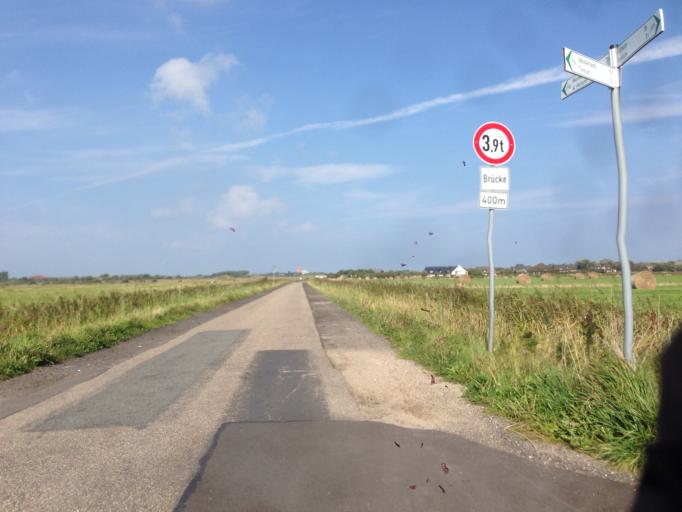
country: DE
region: Schleswig-Holstein
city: Keitum
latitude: 54.8869
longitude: 8.3513
